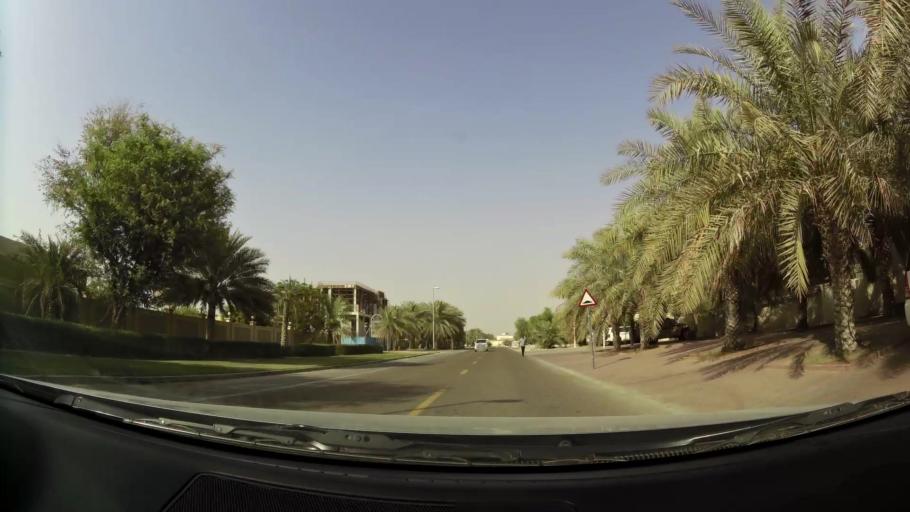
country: AE
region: Dubai
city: Dubai
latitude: 25.1473
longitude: 55.3226
